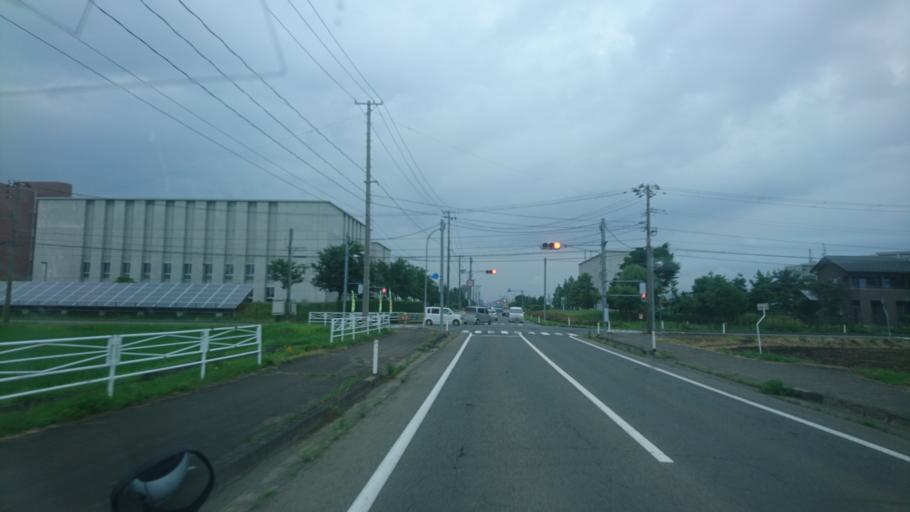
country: JP
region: Iwate
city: Morioka-shi
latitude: 39.6087
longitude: 141.1644
